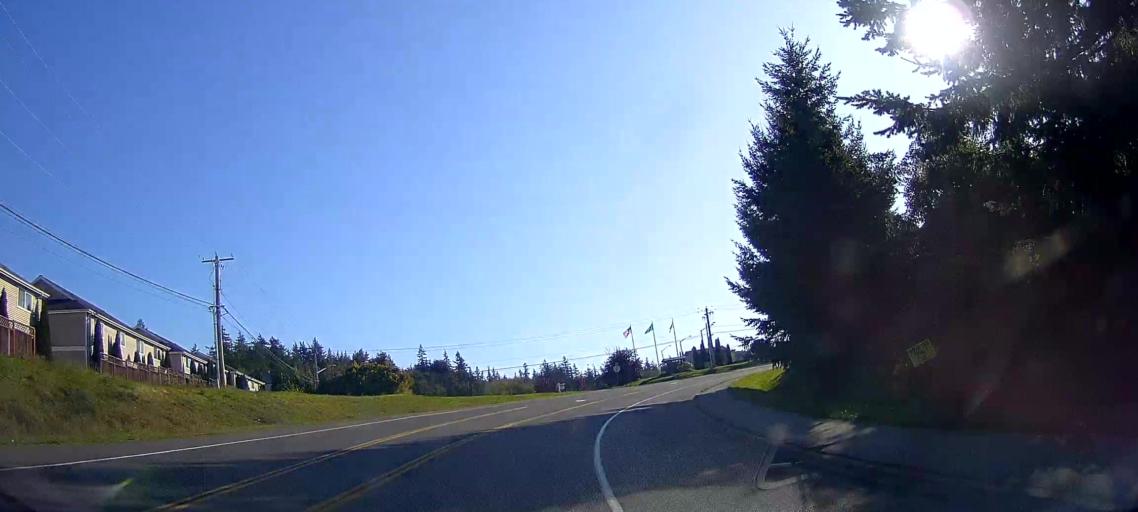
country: US
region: Washington
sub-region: Skagit County
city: Anacortes
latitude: 48.4932
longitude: -122.6317
